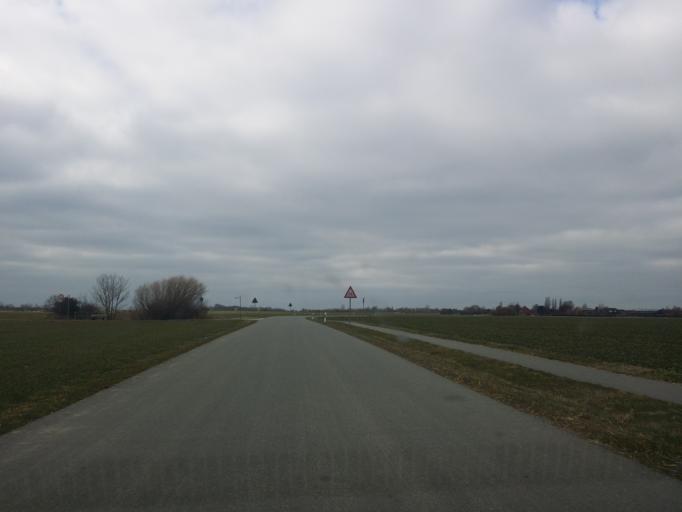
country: DE
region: Schleswig-Holstein
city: Grossenbrode
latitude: 54.4859
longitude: 11.0413
